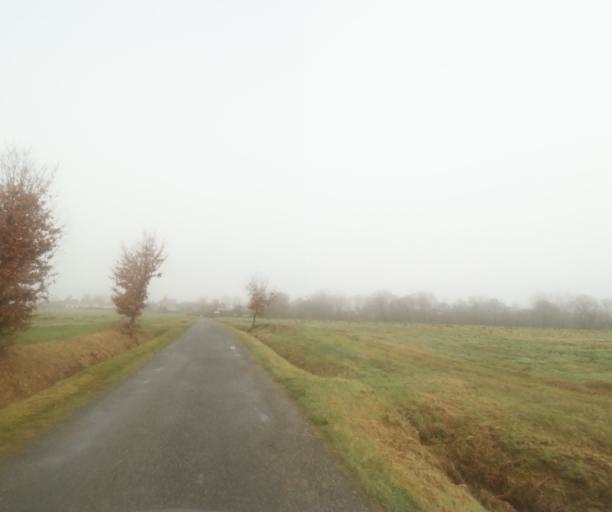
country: FR
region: Midi-Pyrenees
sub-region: Departement de la Haute-Garonne
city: Villaudric
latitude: 43.8375
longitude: 1.4568
